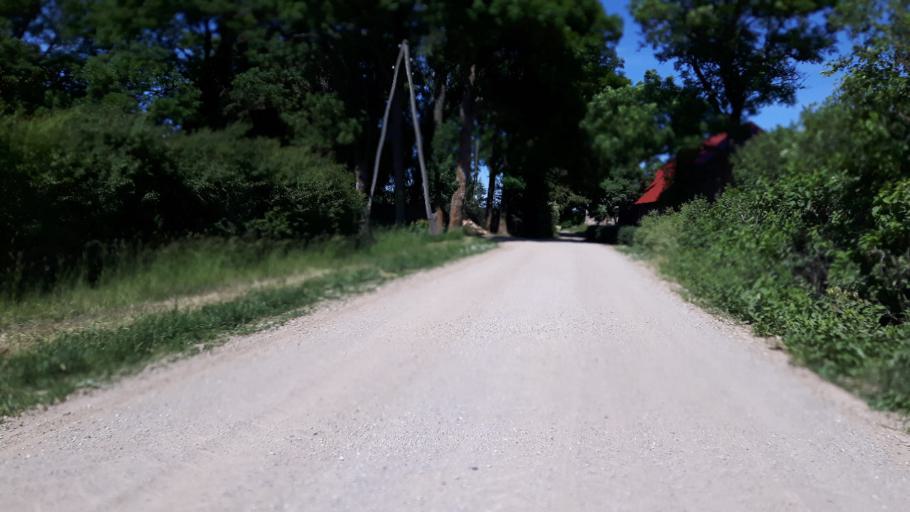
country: LV
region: Kandava
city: Kandava
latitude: 57.0435
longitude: 22.8782
